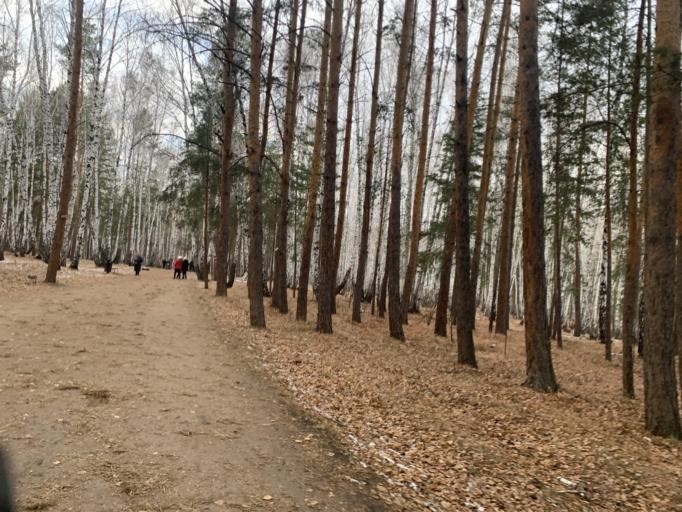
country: RU
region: Chelyabinsk
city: Roshchino
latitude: 55.1961
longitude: 61.2895
